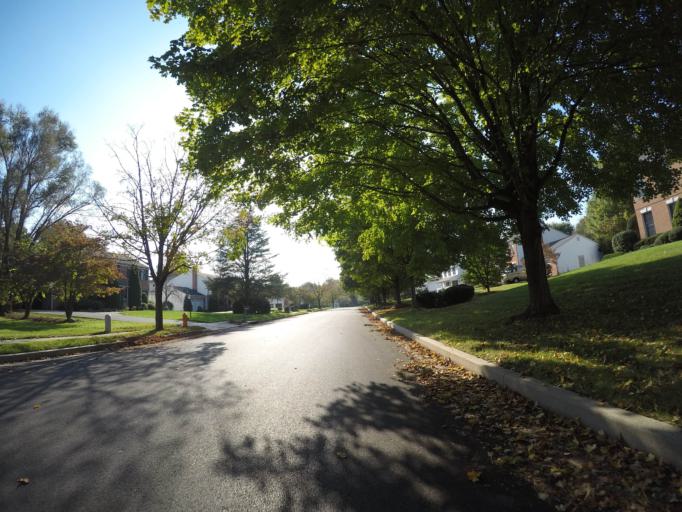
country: US
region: Maryland
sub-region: Howard County
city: Columbia
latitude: 39.2673
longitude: -76.8452
